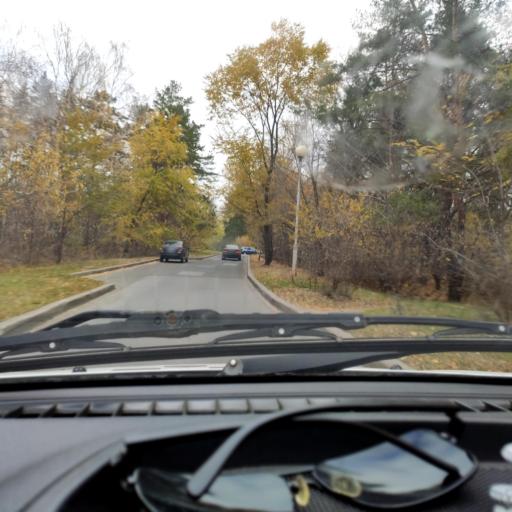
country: RU
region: Samara
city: Zhigulevsk
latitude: 53.4866
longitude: 49.4658
